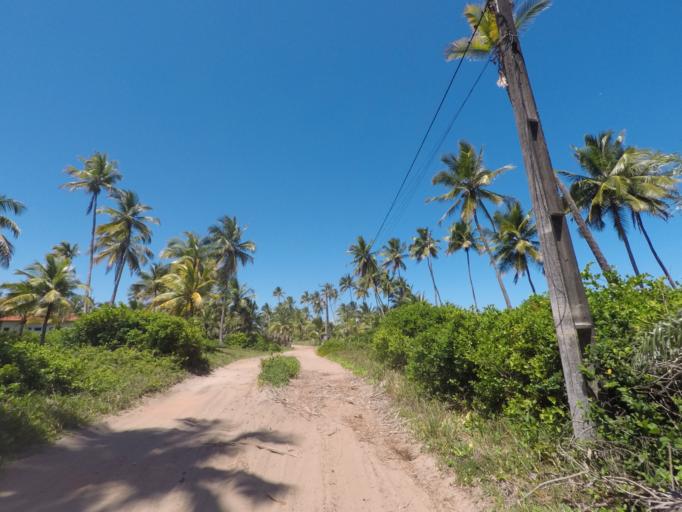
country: BR
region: Bahia
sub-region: Marau
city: Marau
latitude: -14.0006
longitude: -38.9447
